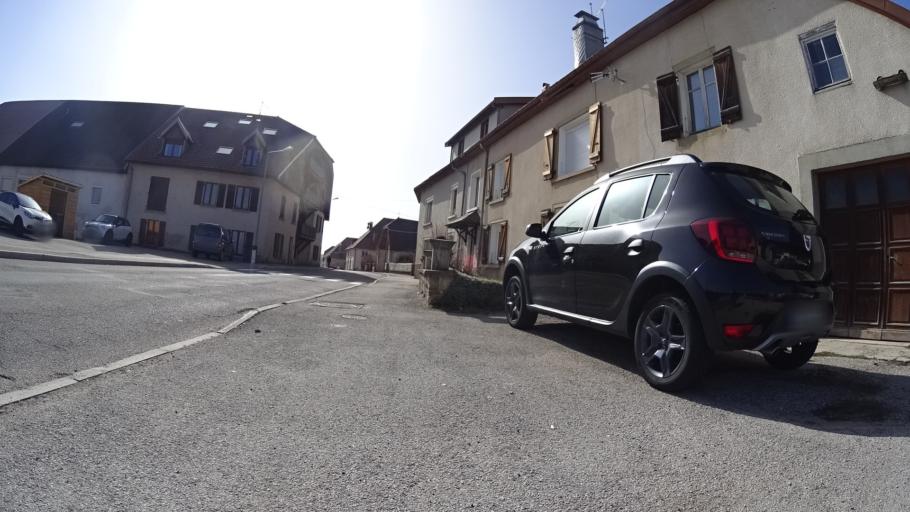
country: FR
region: Franche-Comte
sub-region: Departement du Doubs
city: Frasne
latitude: 46.8531
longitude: 6.1557
